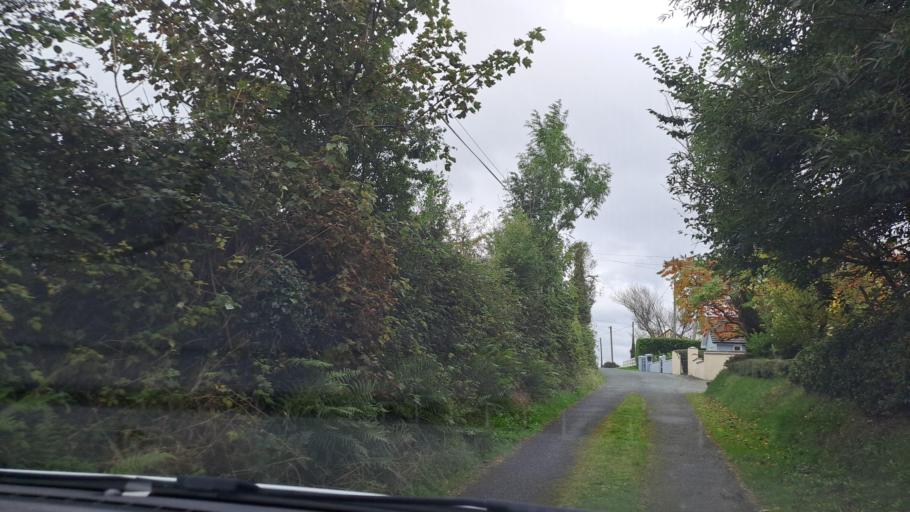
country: IE
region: Ulster
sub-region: An Cabhan
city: Bailieborough
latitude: 54.0013
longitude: -6.9028
